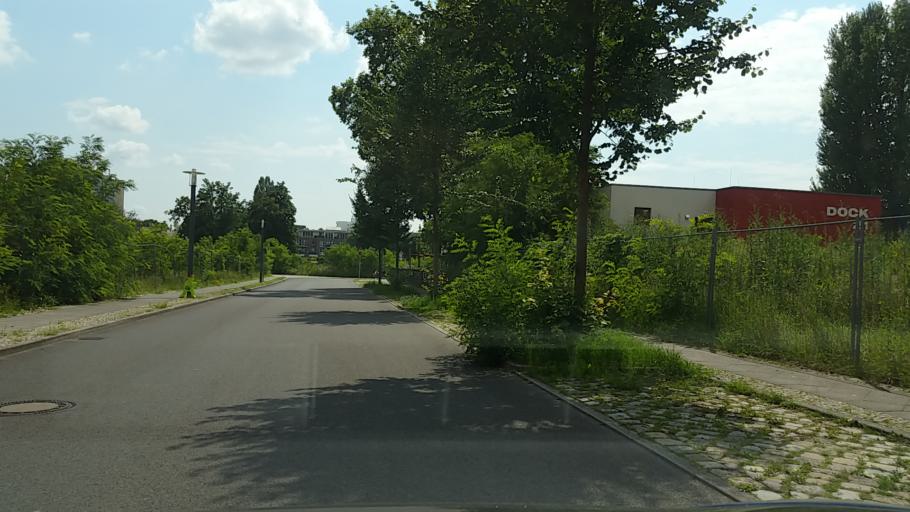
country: DE
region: Berlin
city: Hakenfelde
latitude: 52.5565
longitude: 13.2134
